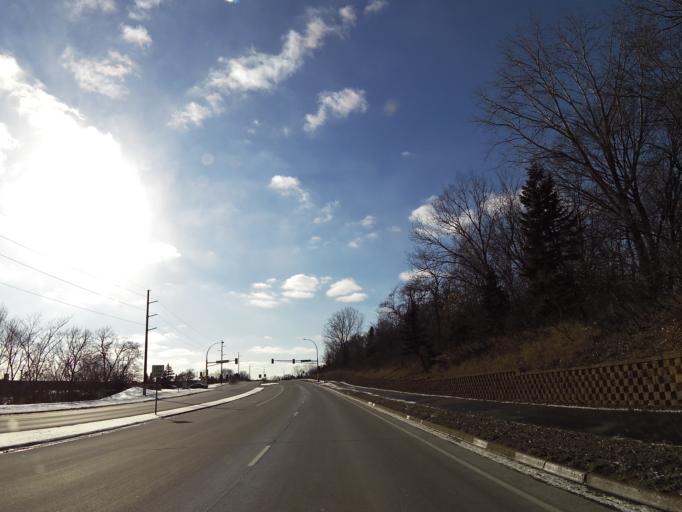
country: US
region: Minnesota
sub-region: Dakota County
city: Burnsville
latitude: 44.7532
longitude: -93.2819
